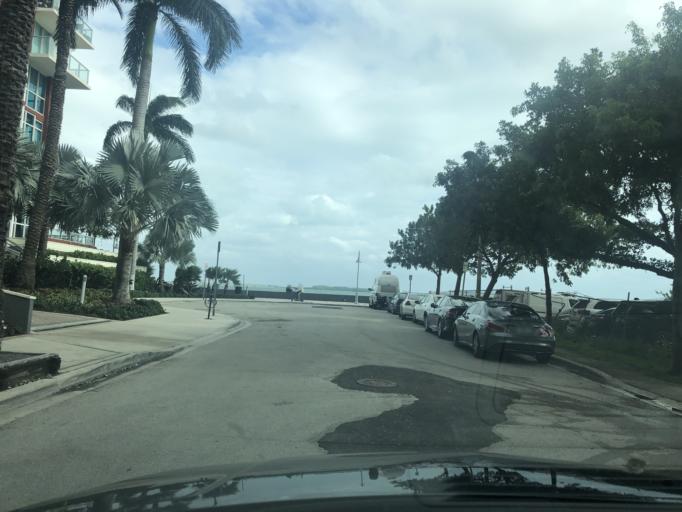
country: US
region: Florida
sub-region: Miami-Dade County
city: Miami
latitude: 25.7617
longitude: -80.1893
